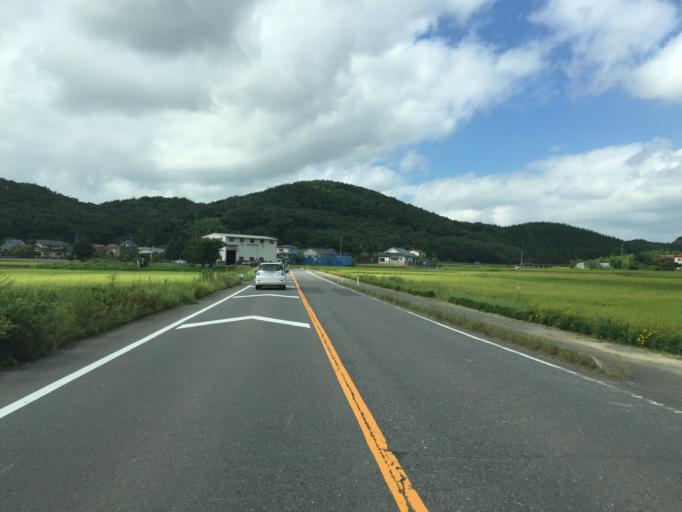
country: JP
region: Fukushima
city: Motomiya
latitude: 37.4921
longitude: 140.3729
